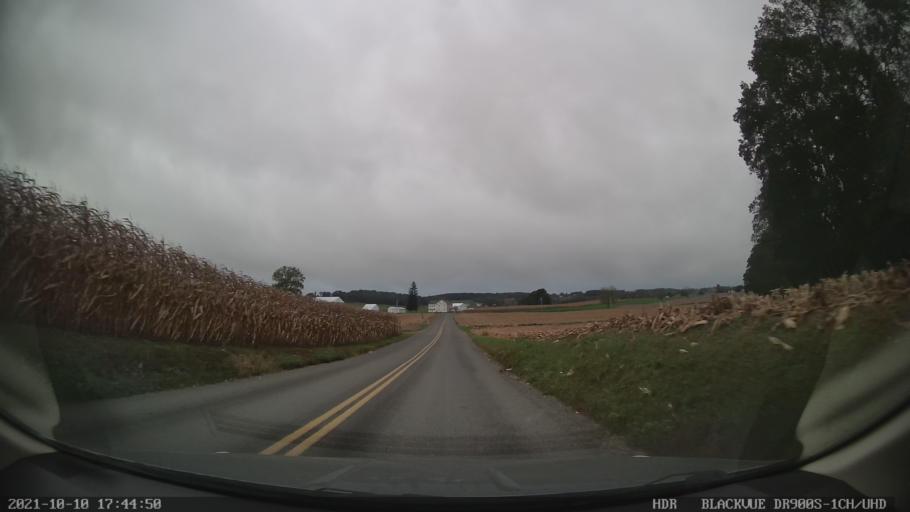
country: US
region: Pennsylvania
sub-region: Lehigh County
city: Breinigsville
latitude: 40.5480
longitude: -75.6778
